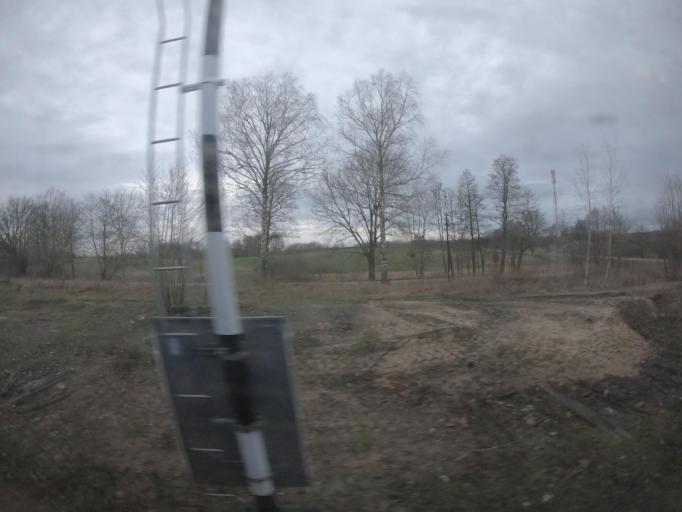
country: PL
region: West Pomeranian Voivodeship
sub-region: Powiat szczecinecki
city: Borne Sulinowo
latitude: 53.6346
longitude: 16.4907
